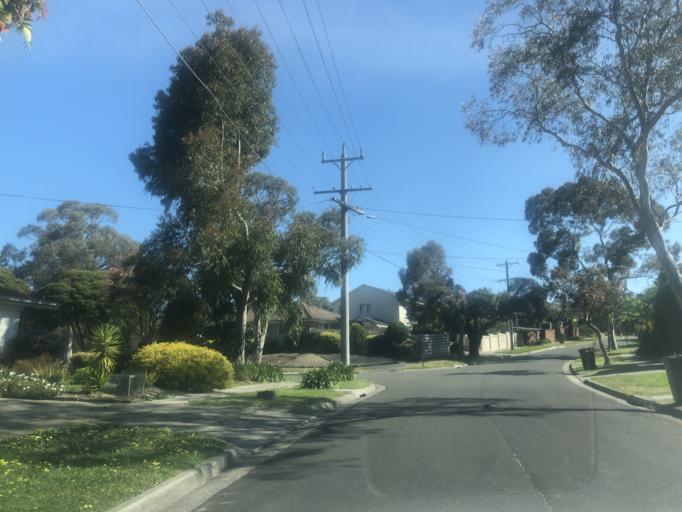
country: AU
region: Victoria
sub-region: Monash
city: Mulgrave
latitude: -37.9044
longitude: 145.1978
